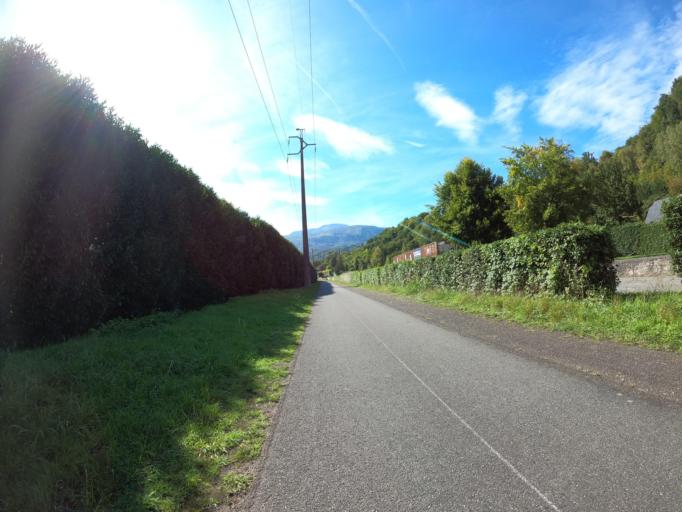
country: FR
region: Midi-Pyrenees
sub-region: Departement des Hautes-Pyrenees
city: Argeles-Gazost
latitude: 43.0154
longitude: -0.0974
